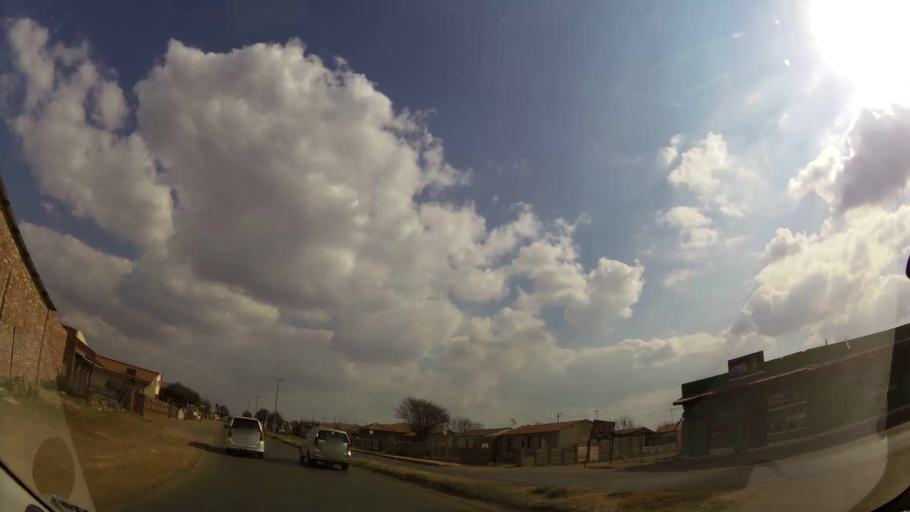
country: ZA
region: Gauteng
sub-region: Ekurhuleni Metropolitan Municipality
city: Springs
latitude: -26.1321
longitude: 28.4352
